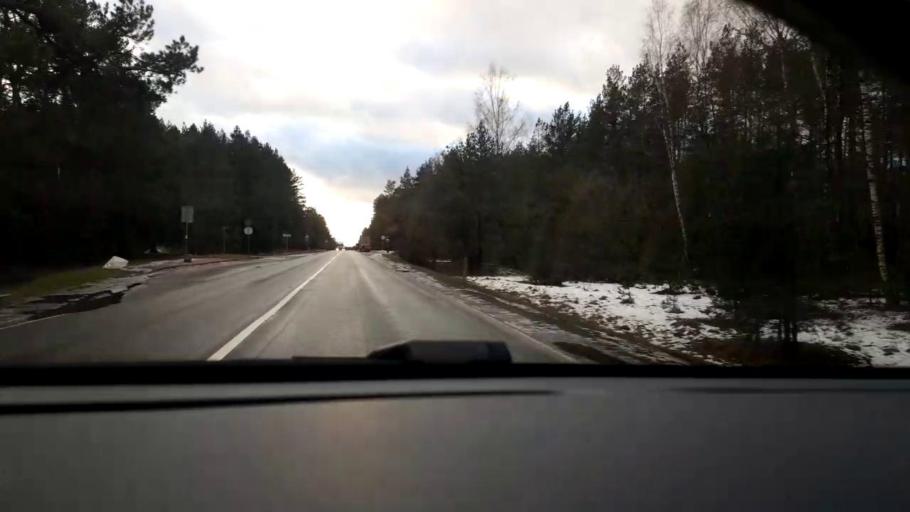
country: LT
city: Nemencine
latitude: 54.7947
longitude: 25.3919
